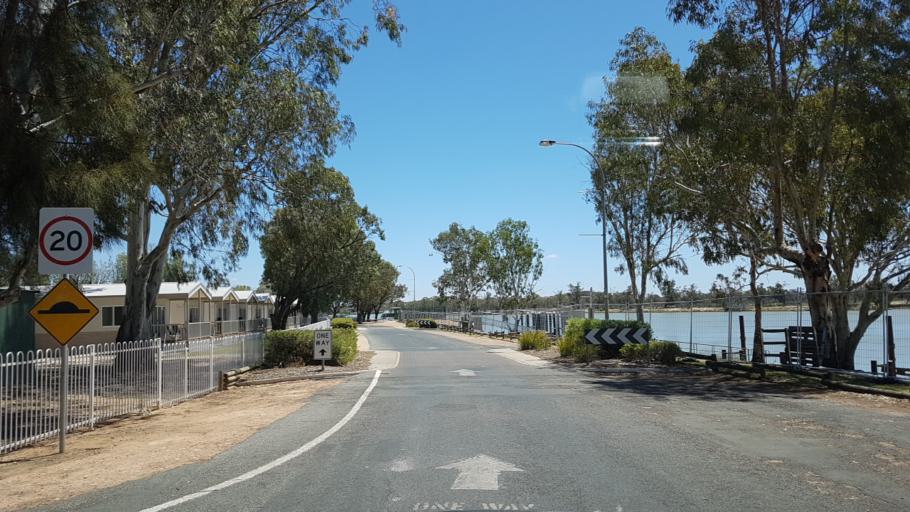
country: AU
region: South Australia
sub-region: Loxton Waikerie
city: Waikerie
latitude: -34.1739
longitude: 139.9837
